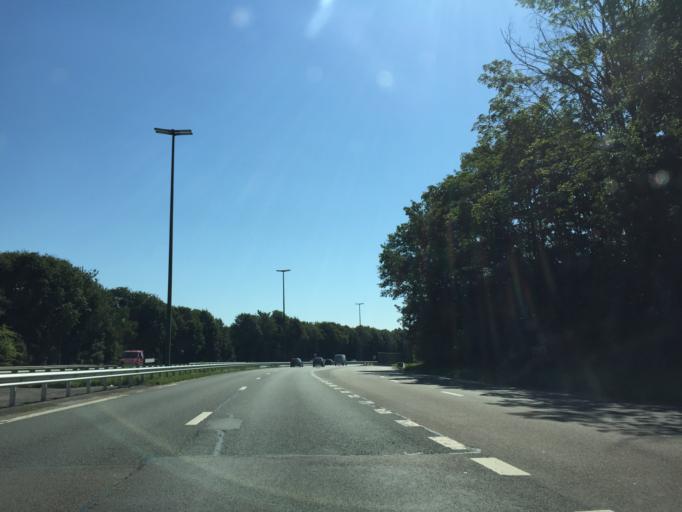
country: BE
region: Wallonia
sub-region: Province de Liege
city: Dison
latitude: 50.6306
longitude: 5.8459
